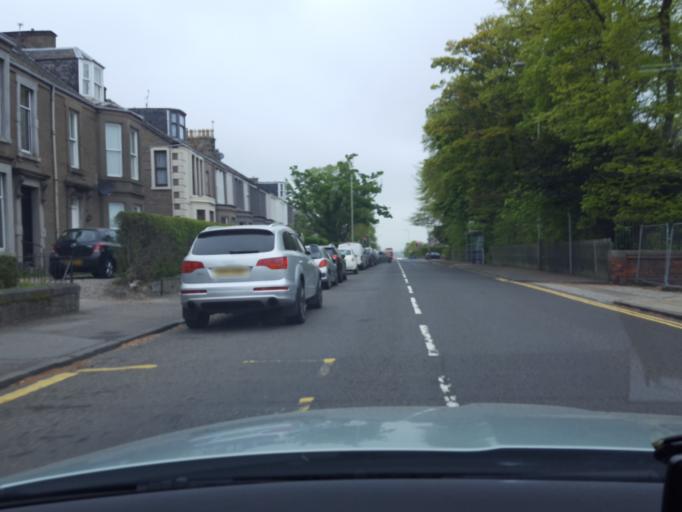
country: GB
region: Scotland
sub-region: Dundee City
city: Dundee
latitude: 56.4766
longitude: -2.9538
